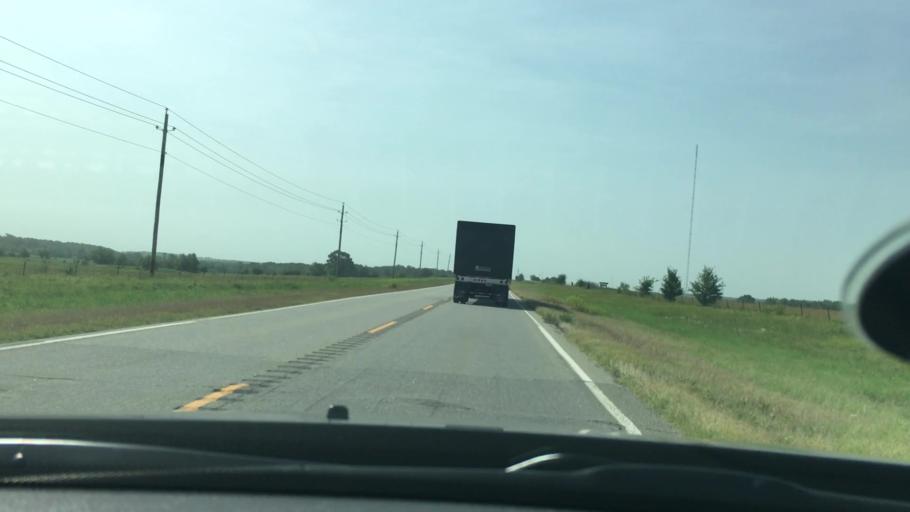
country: US
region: Oklahoma
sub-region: Atoka County
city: Atoka
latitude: 34.4253
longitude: -96.1935
